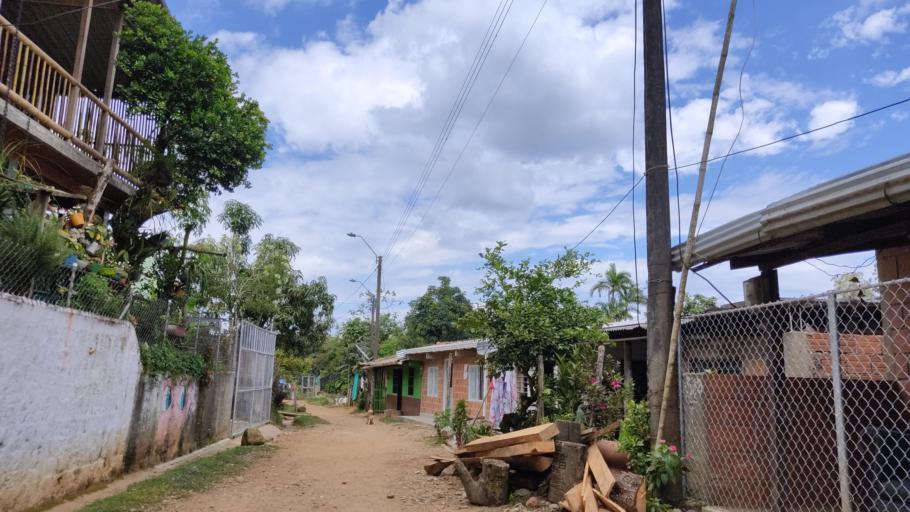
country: CO
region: Valle del Cauca
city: Jamundi
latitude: 3.2103
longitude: -76.6553
